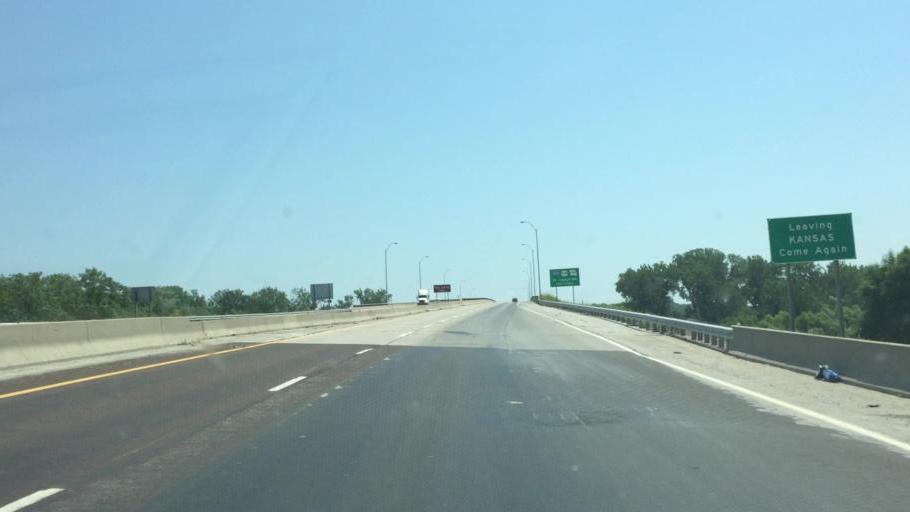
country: US
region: Kansas
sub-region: Doniphan County
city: Elwood
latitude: 39.7493
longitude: -94.8661
